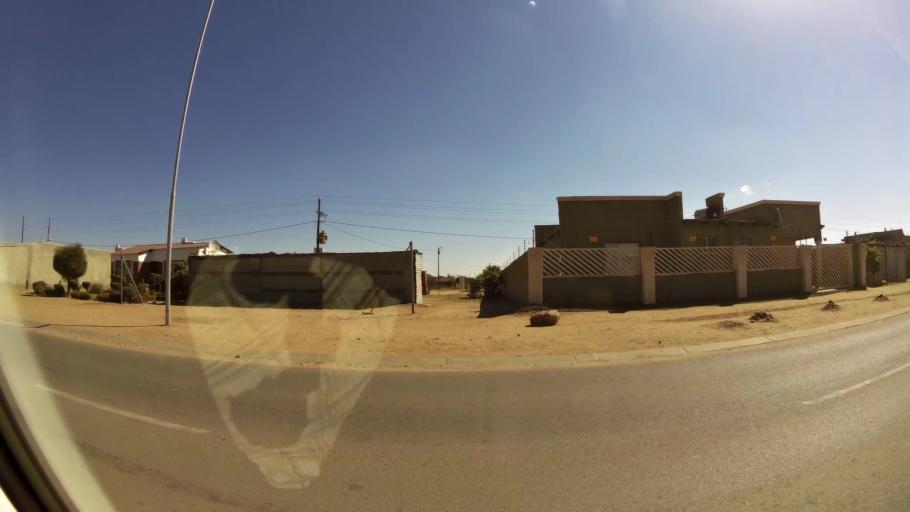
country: ZA
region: Limpopo
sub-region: Capricorn District Municipality
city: Polokwane
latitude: -23.8582
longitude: 29.4123
